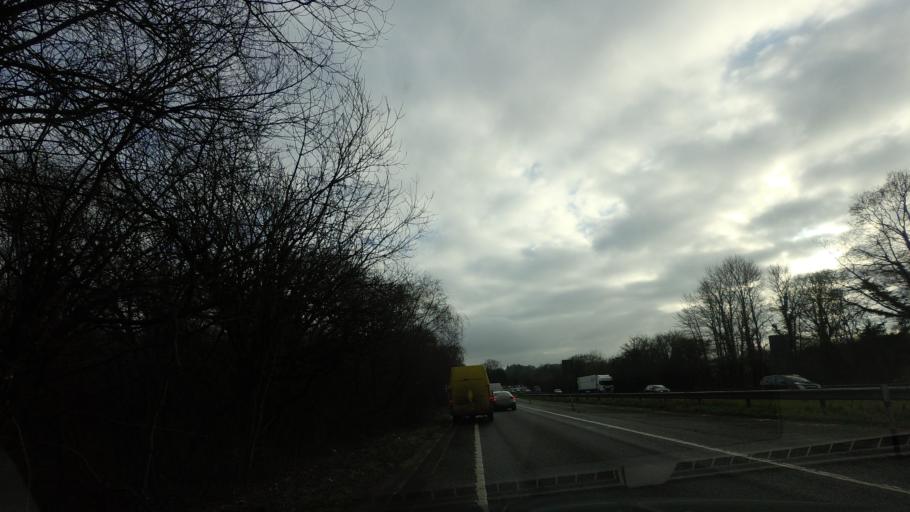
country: GB
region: England
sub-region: Kent
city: Hawkhurst
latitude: 51.0611
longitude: 0.4446
